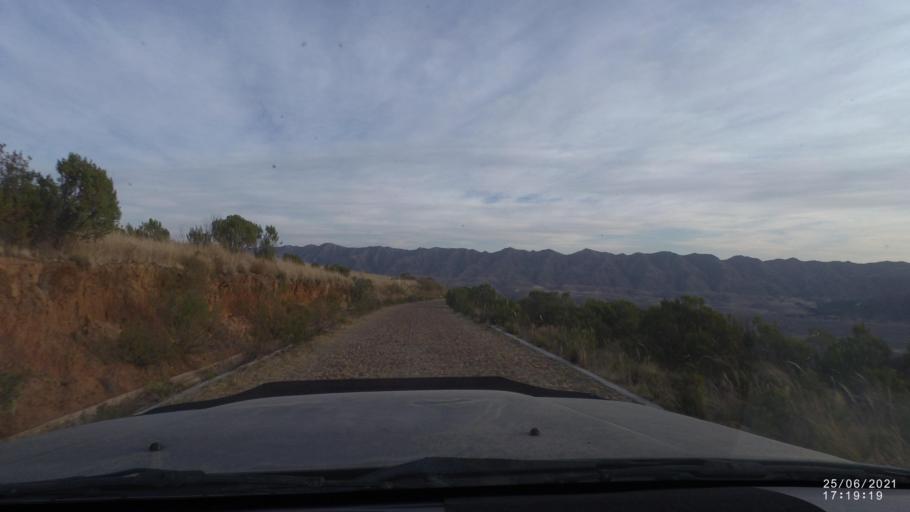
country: BO
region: Cochabamba
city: Arani
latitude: -17.9011
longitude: -65.6928
